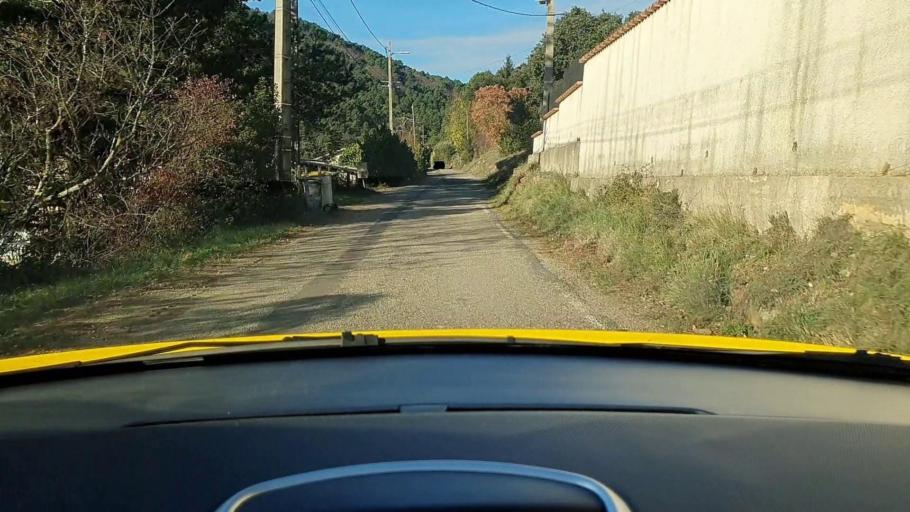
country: FR
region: Languedoc-Roussillon
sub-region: Departement du Gard
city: Branoux-les-Taillades
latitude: 44.2239
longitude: 3.9912
